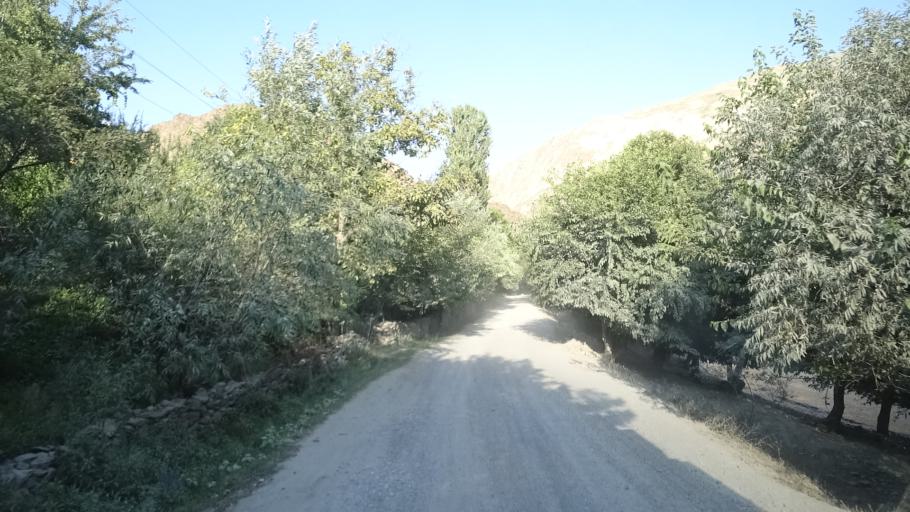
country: AF
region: Badakhshan
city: Maymay
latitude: 38.4780
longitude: 70.9595
